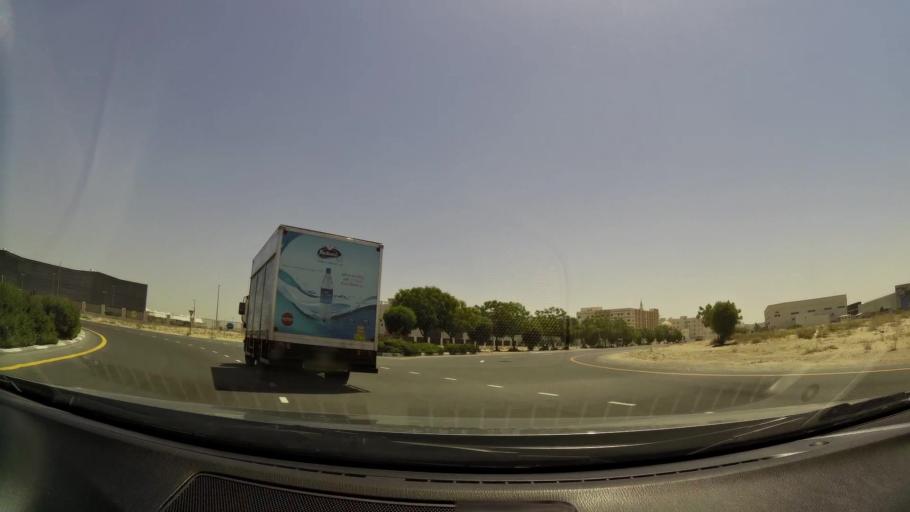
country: AE
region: Dubai
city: Dubai
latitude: 24.9731
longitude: 55.1974
